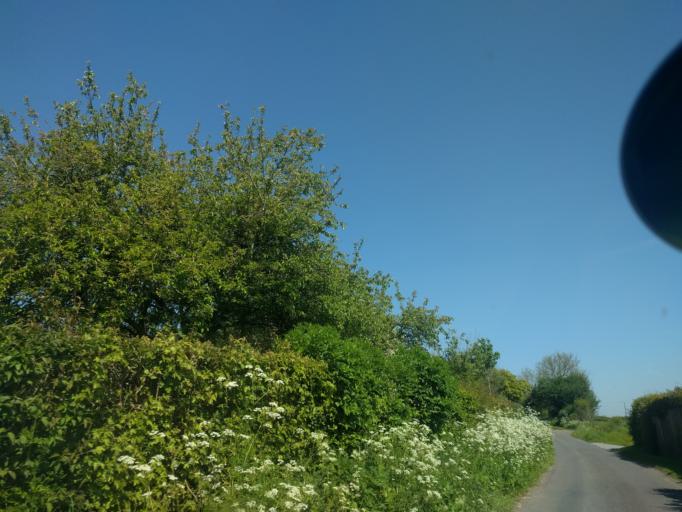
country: GB
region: England
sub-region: Somerset
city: Langport
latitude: 51.0449
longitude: -2.8039
